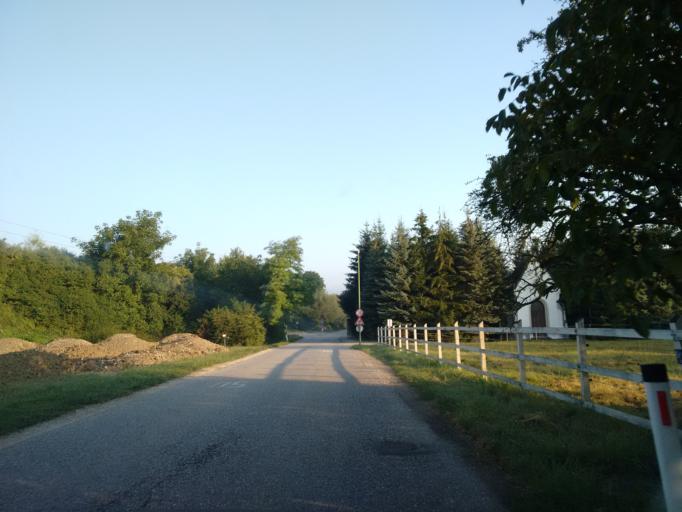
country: AT
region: Upper Austria
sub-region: Wels Stadt
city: Wels
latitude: 48.1851
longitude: 14.0032
